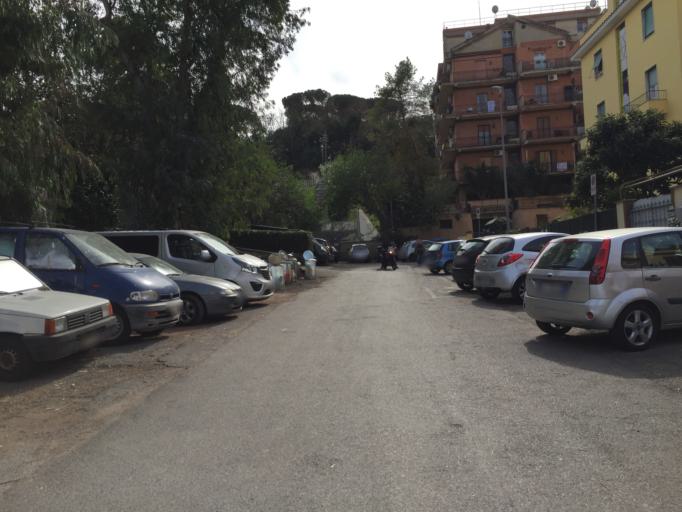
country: VA
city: Vatican City
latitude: 41.8957
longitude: 12.4540
